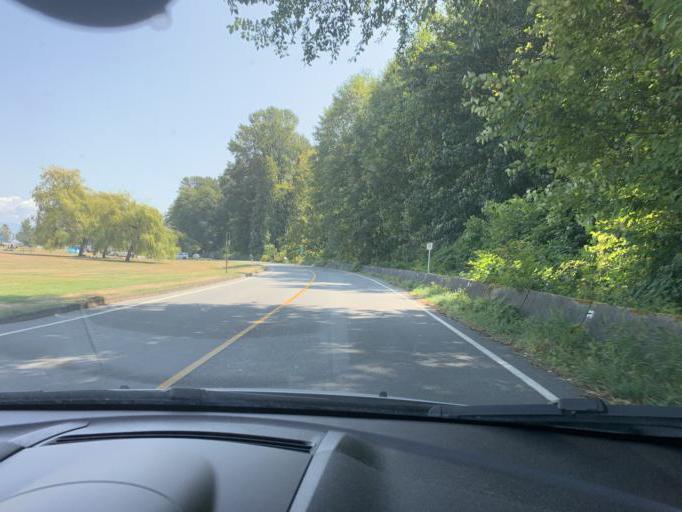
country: CA
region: British Columbia
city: West End
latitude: 49.2783
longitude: -123.2349
